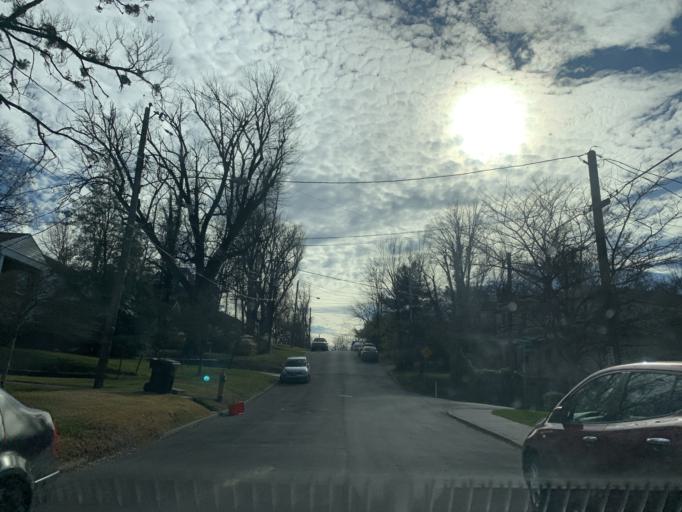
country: US
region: Kentucky
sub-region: Jefferson County
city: Indian Hills
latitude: 38.2519
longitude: -85.6995
